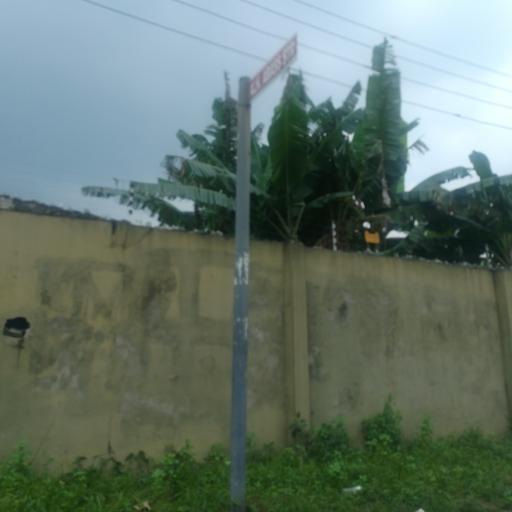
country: NG
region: Lagos
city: Ojota
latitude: 6.5735
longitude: 3.3930
